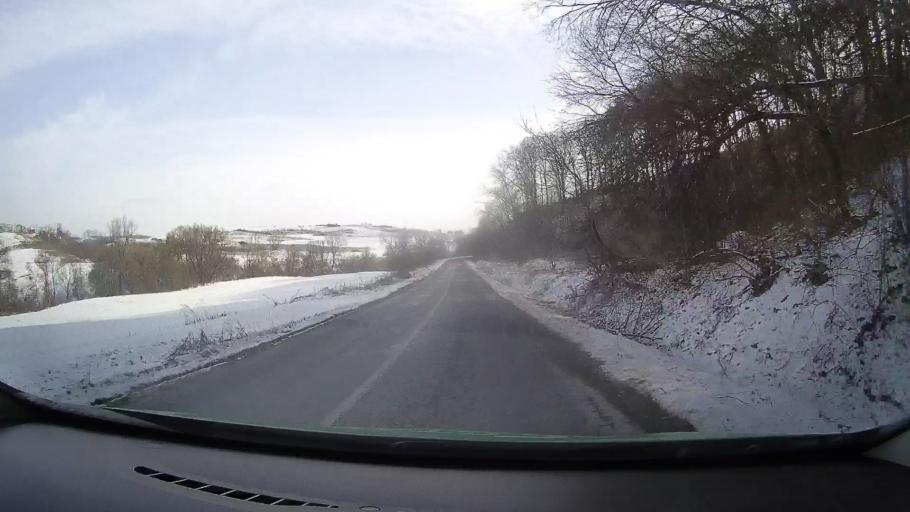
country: RO
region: Mures
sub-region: Comuna Apold
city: Saes
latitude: 46.1713
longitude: 24.7566
